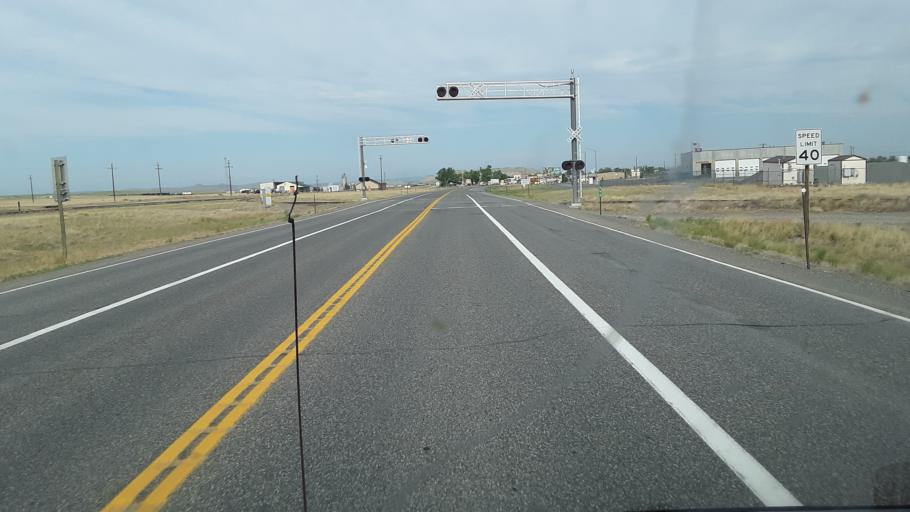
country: US
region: Wyoming
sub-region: Fremont County
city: Riverton
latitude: 43.2361
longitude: -108.0972
